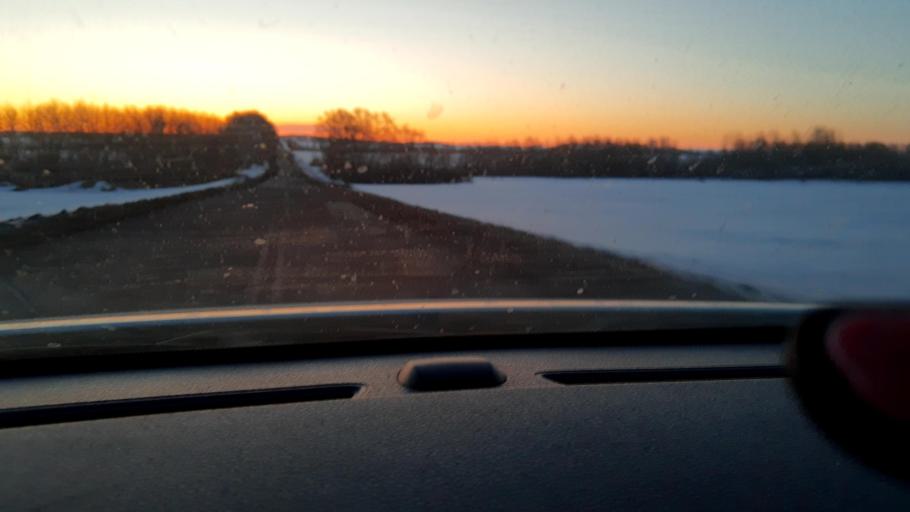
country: RU
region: Bashkortostan
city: Avdon
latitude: 54.3877
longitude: 55.7395
